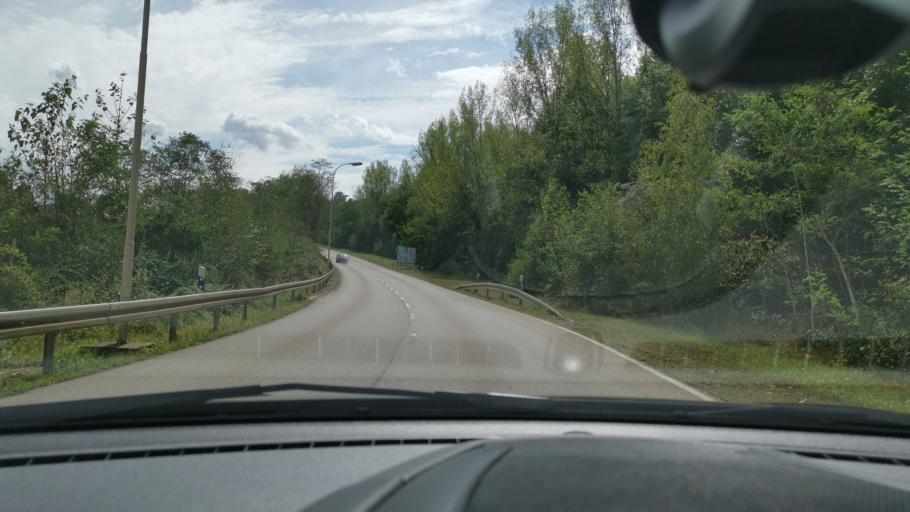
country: DE
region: North Rhine-Westphalia
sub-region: Regierungsbezirk Dusseldorf
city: Grevenbroich
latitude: 51.0560
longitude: 6.5571
